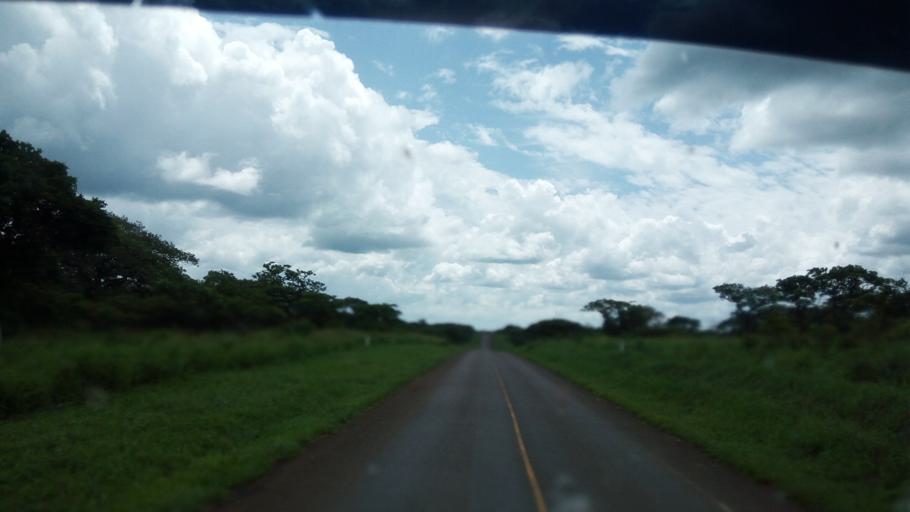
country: UG
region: Northern Region
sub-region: Oyam District
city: Oyam
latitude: 2.2957
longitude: 32.1968
